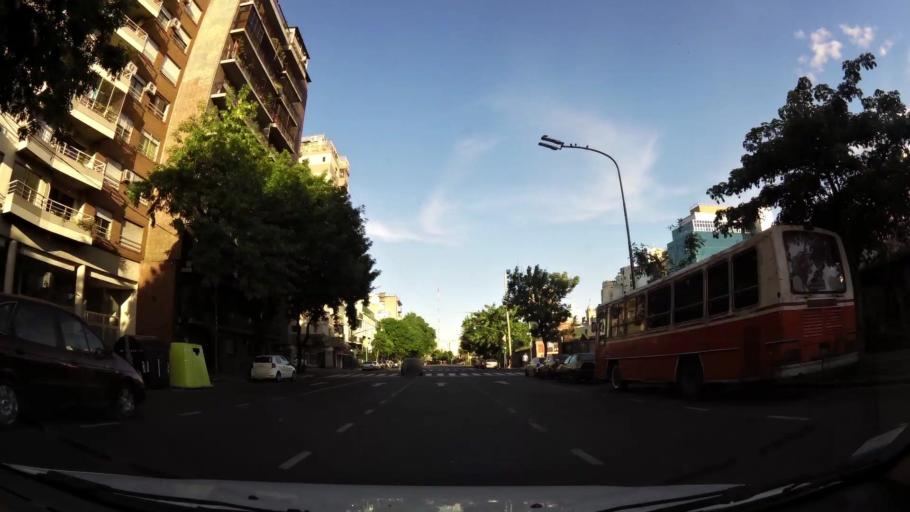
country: AR
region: Buenos Aires F.D.
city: Buenos Aires
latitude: -34.6086
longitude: -58.4179
